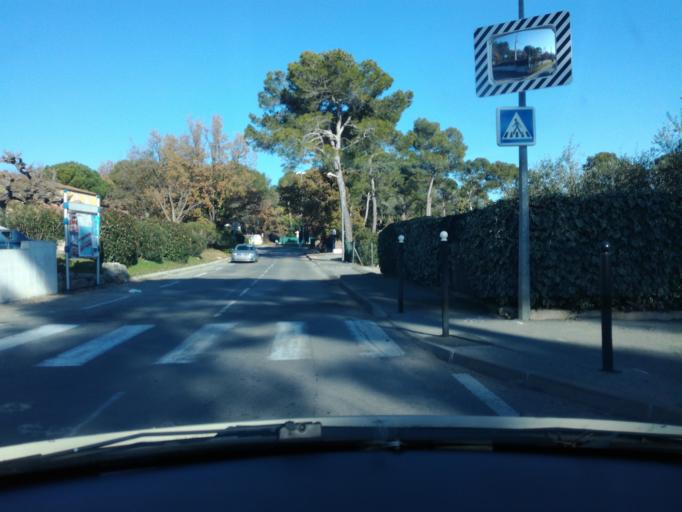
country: FR
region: Provence-Alpes-Cote d'Azur
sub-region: Departement des Alpes-Maritimes
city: La Roquette-sur-Siagne
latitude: 43.6059
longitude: 6.9556
